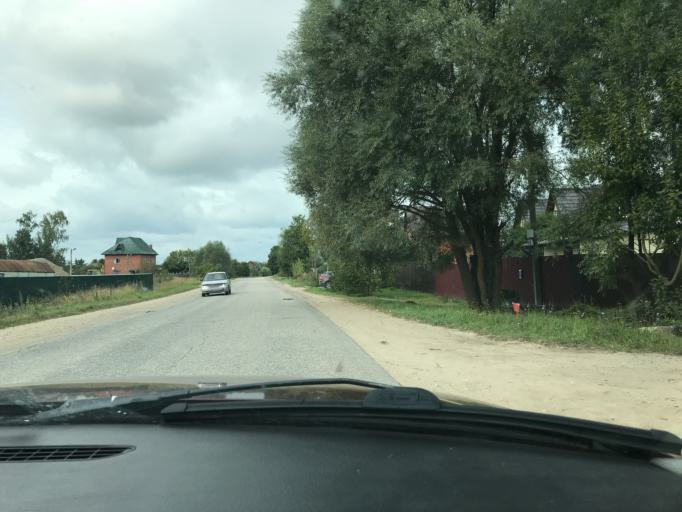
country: RU
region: Kaluga
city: Maloyaroslavets
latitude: 54.9864
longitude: 36.4715
